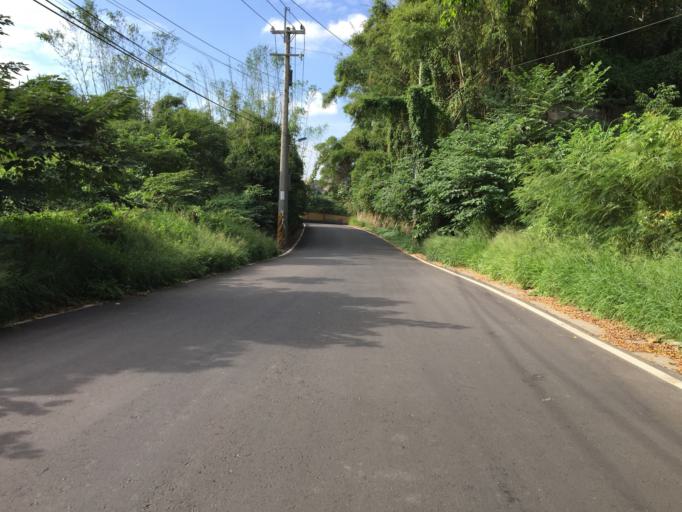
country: TW
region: Taiwan
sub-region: Hsinchu
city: Hsinchu
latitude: 24.7696
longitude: 120.9380
